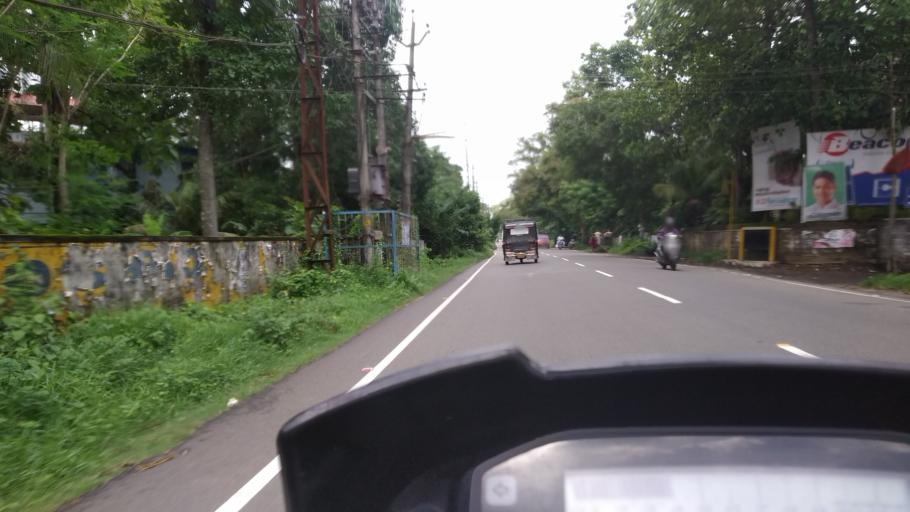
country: IN
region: Kerala
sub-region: Ernakulam
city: Elur
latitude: 10.1386
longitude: 76.2670
